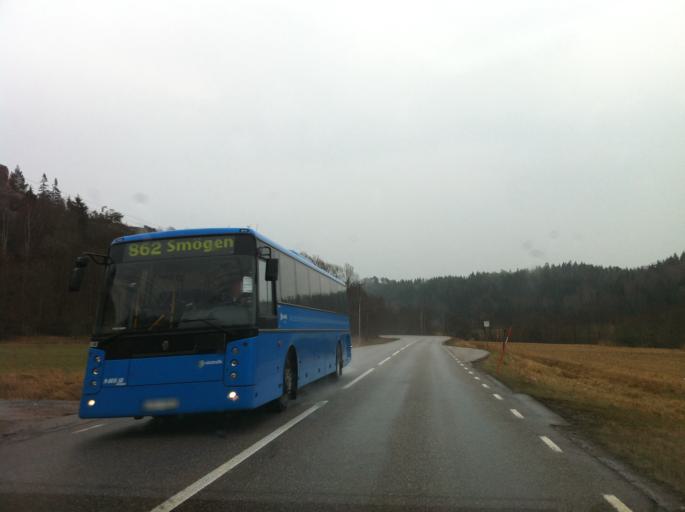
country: SE
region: Vaestra Goetaland
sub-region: Lysekils Kommun
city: Brastad
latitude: 58.4563
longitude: 11.4658
